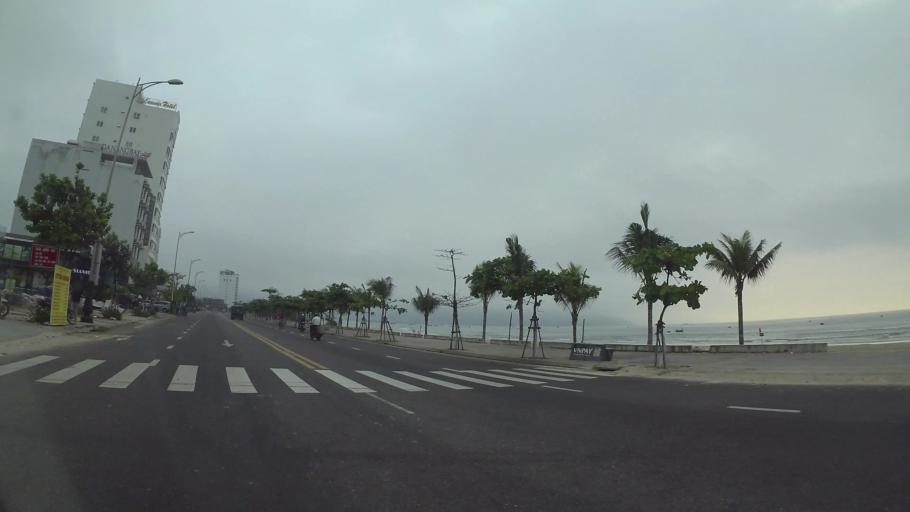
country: VN
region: Da Nang
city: Son Tra
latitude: 16.0848
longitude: 108.2481
